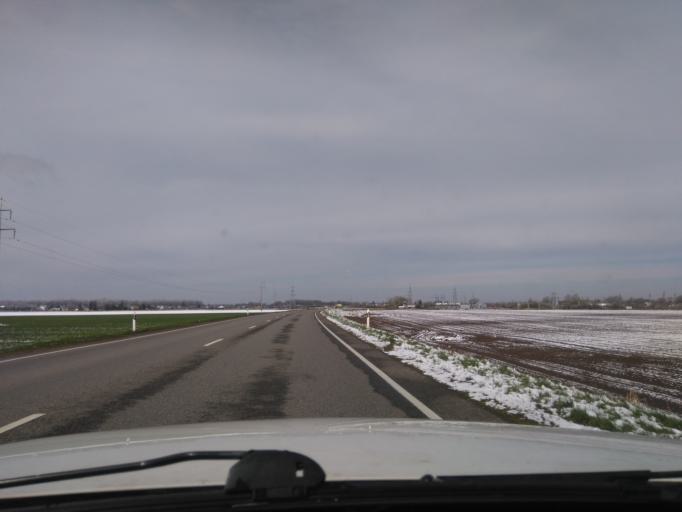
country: LT
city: Vilkaviskis
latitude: 54.6321
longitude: 23.0332
